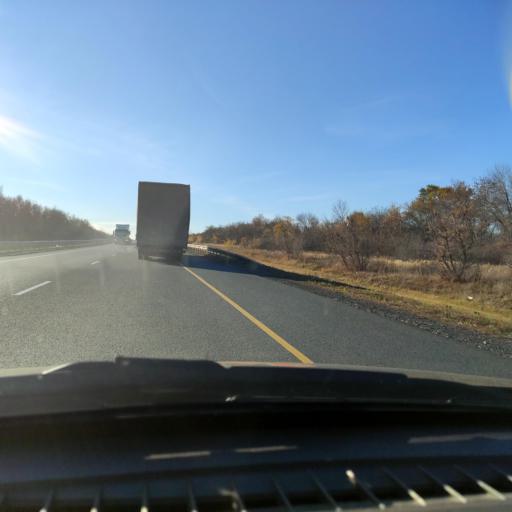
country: RU
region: Samara
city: Obsharovka
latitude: 53.2256
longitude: 48.8839
